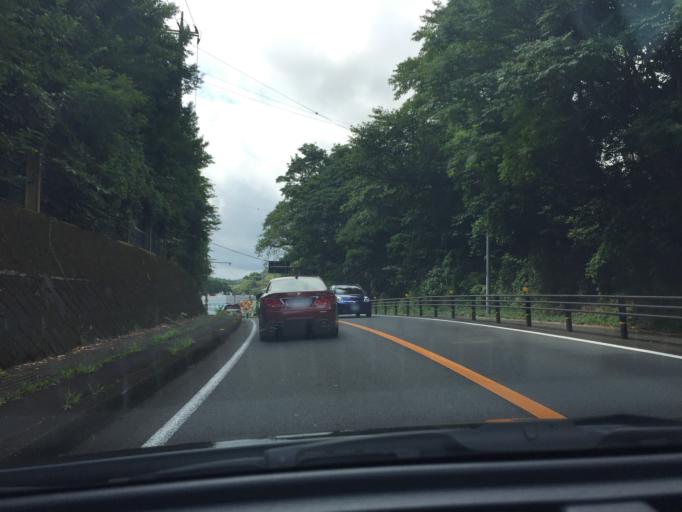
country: JP
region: Shizuoka
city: Ito
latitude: 34.9556
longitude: 139.1167
